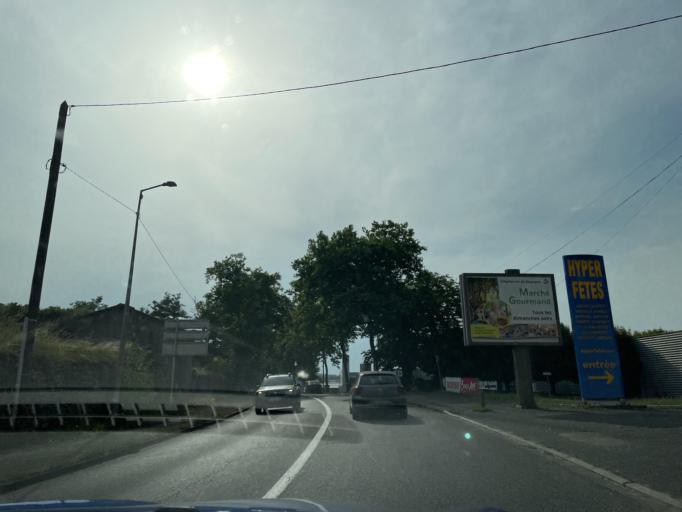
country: FR
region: Midi-Pyrenees
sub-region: Departement de l'Aveyron
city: Villefranche-de-Rouergue
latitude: 44.3603
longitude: 2.0178
